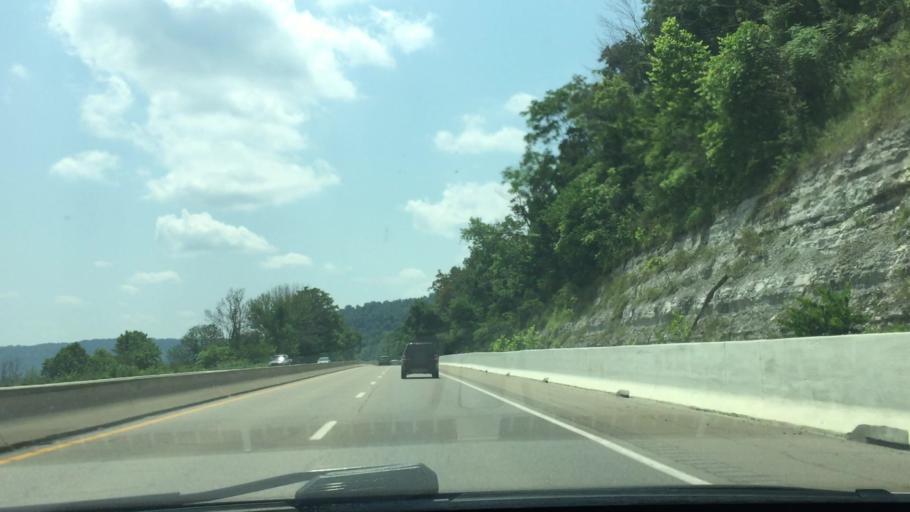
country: US
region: West Virginia
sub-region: Marshall County
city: Glendale
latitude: 39.9382
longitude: -80.7635
